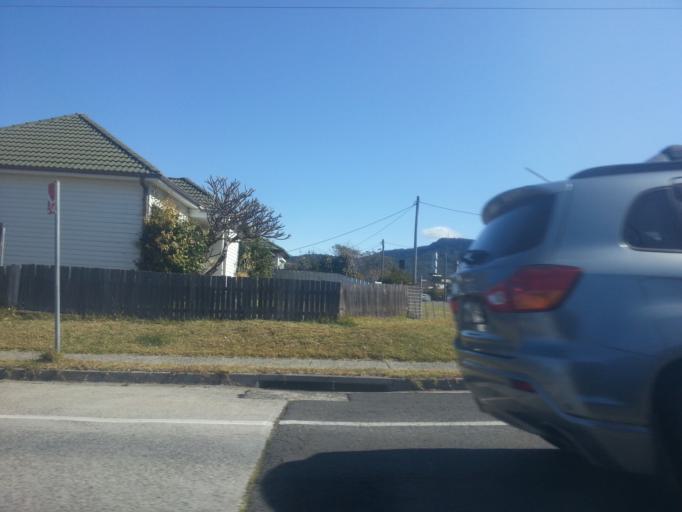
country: AU
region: New South Wales
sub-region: Wollongong
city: East Corrimal
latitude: -34.3800
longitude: 150.9079
